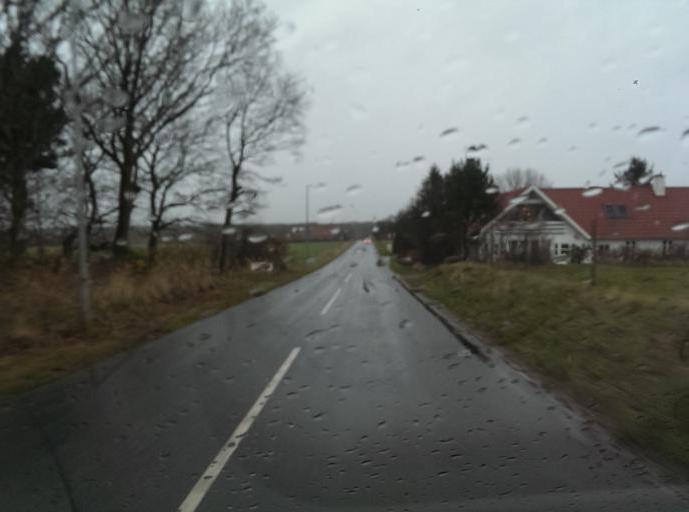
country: DK
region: South Denmark
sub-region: Esbjerg Kommune
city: Tjaereborg
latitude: 55.4729
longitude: 8.5775
